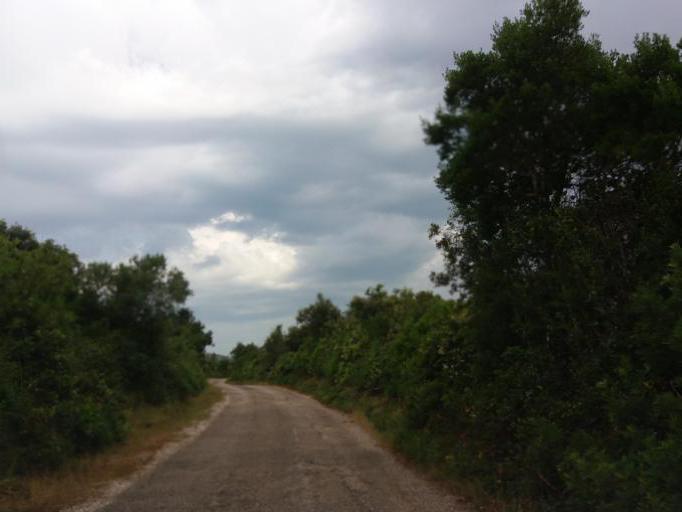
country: HR
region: Zadarska
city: Sali
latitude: 43.9081
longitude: 15.1401
